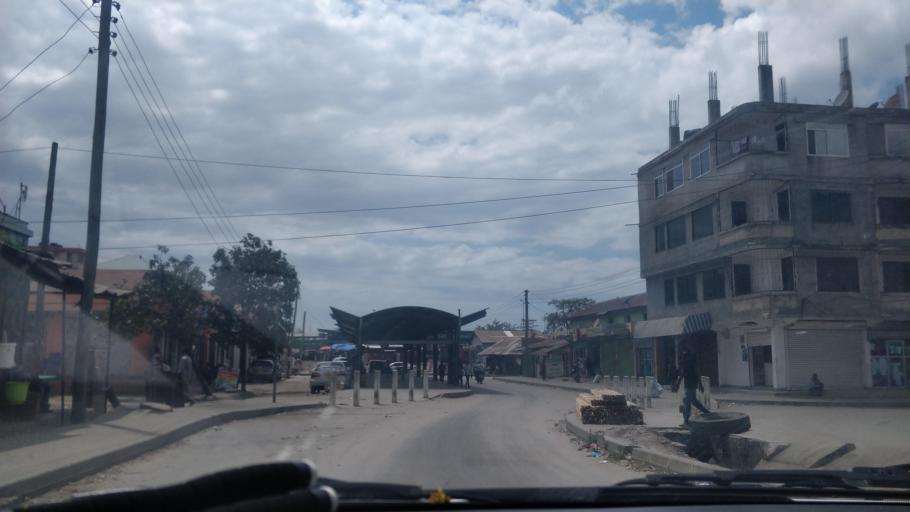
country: TZ
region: Dar es Salaam
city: Magomeni
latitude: -6.8094
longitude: 39.2598
